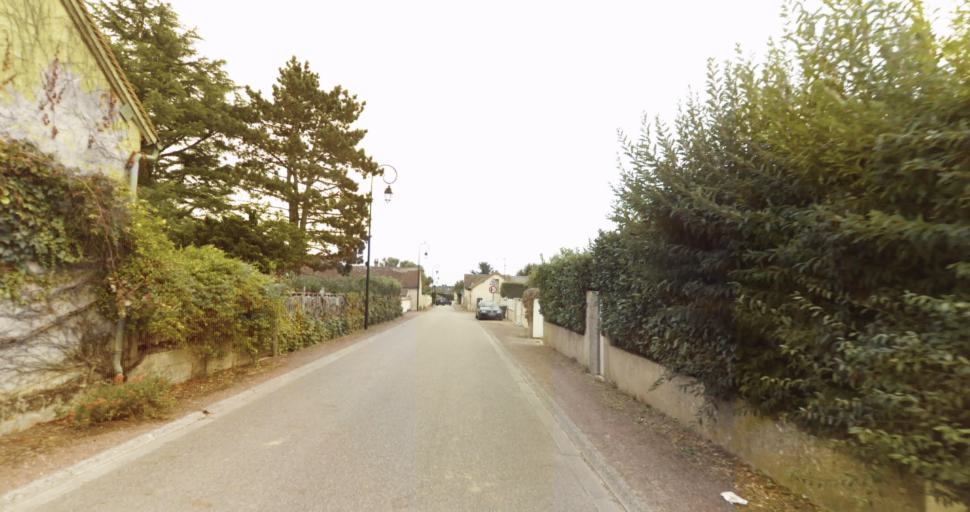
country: FR
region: Haute-Normandie
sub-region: Departement de l'Eure
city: Menilles
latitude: 48.9592
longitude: 1.2931
